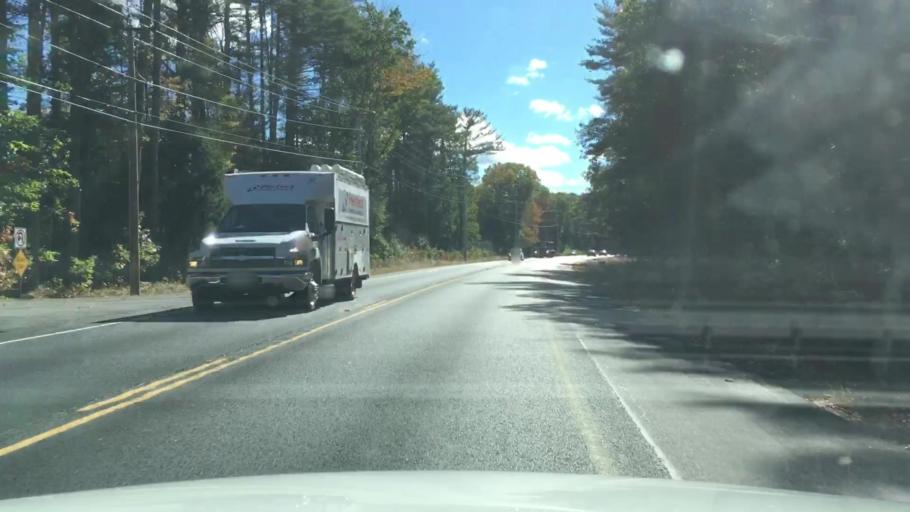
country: US
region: Maine
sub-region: York County
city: South Sanford
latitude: 43.4275
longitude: -70.7329
